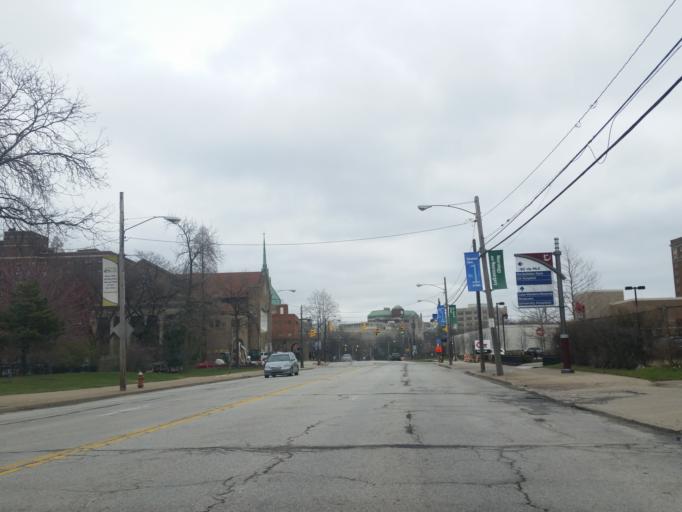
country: US
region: Ohio
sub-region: Cuyahoga County
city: Bratenahl
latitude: 41.5054
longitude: -81.6167
